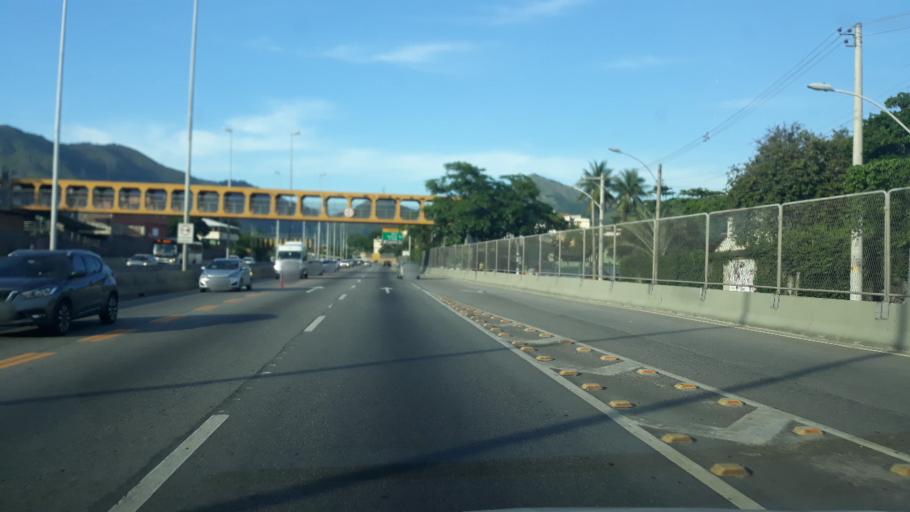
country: BR
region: Rio de Janeiro
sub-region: Rio De Janeiro
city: Rio de Janeiro
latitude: -22.8903
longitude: -43.2968
